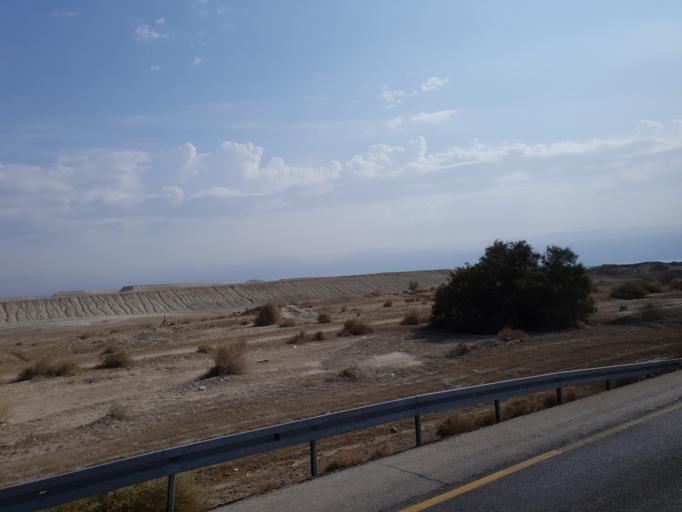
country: PS
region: West Bank
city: Jericho
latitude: 31.7946
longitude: 35.4965
